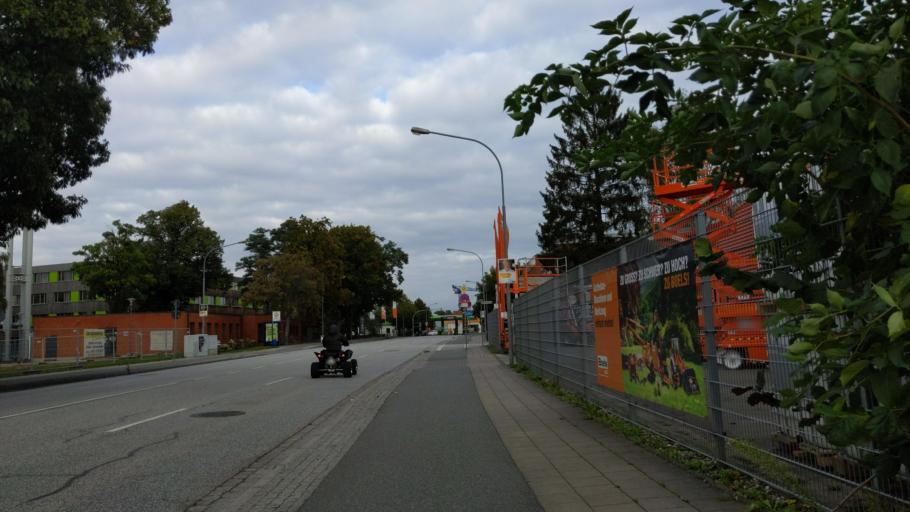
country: DE
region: Schleswig-Holstein
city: Luebeck
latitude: 53.8483
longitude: 10.6726
